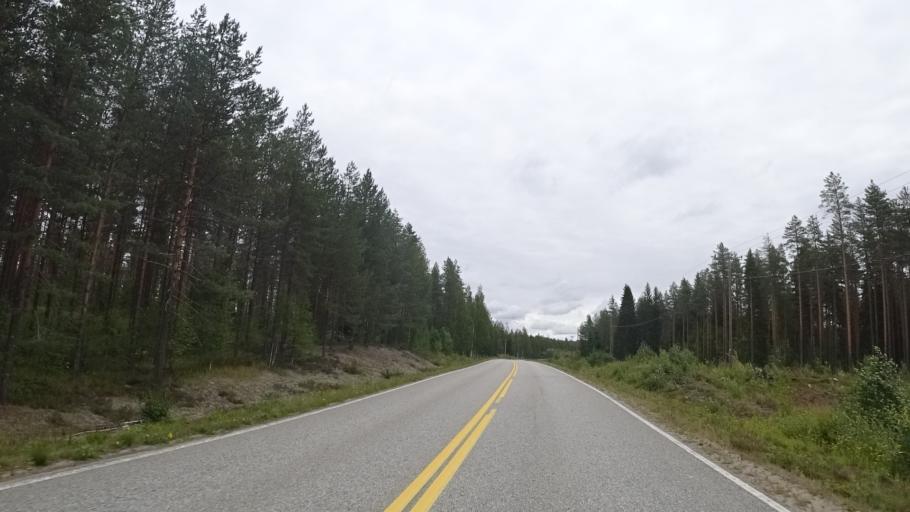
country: FI
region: North Karelia
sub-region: Joensuu
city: Ilomantsi
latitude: 62.6257
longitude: 31.2555
